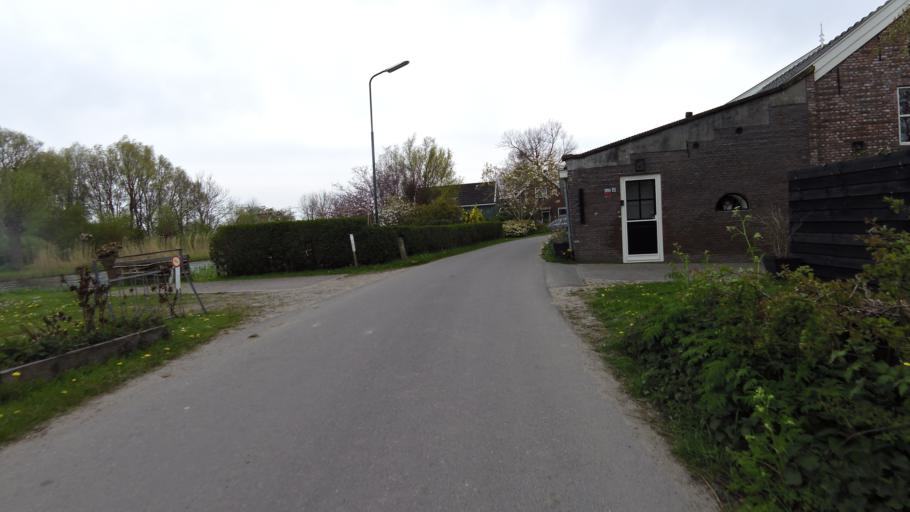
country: NL
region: North Holland
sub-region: Gemeente Amsterdam
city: Driemond
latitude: 52.2881
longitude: 5.0034
